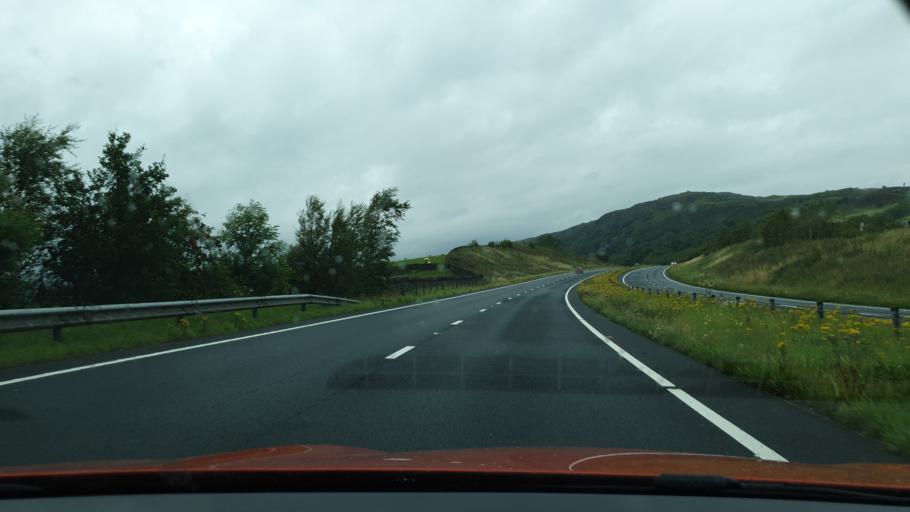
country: GB
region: England
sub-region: Cumbria
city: Grange-over-Sands
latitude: 54.2392
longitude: -2.9261
